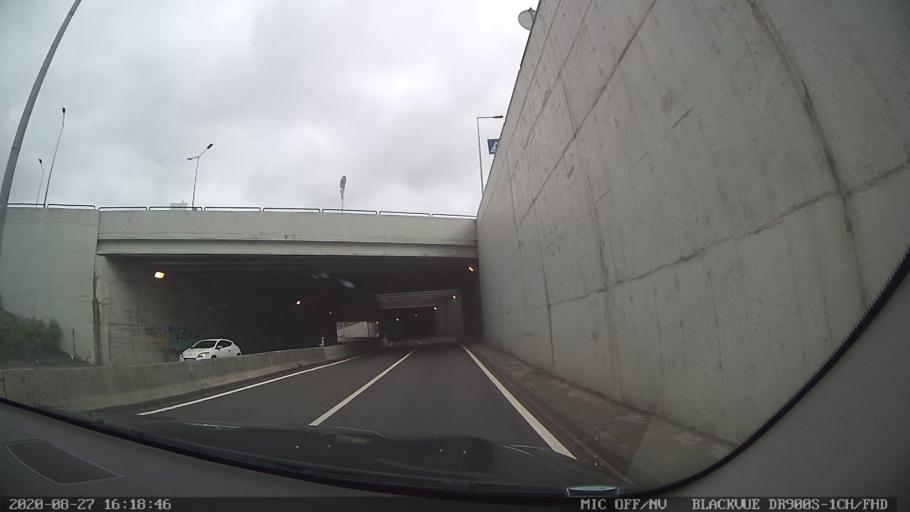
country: PT
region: Leiria
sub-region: Leiria
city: Leiria
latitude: 39.7344
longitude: -8.8091
